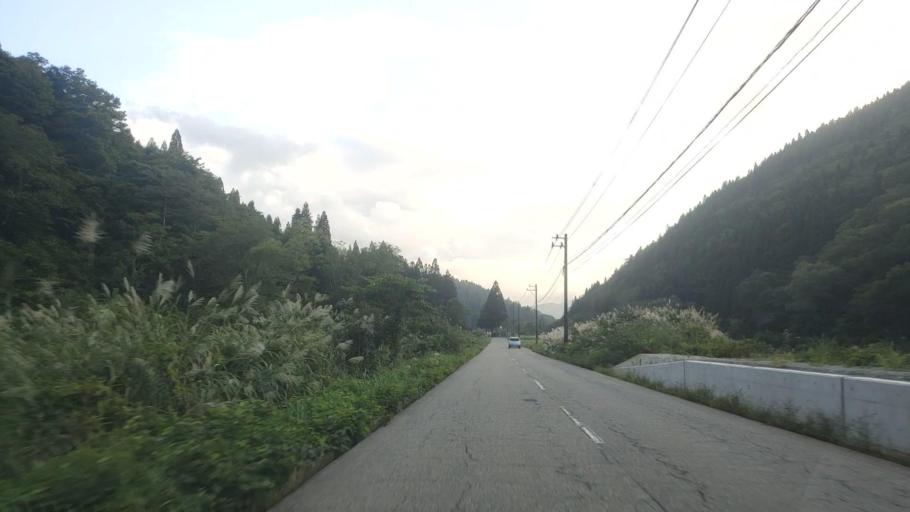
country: JP
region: Toyama
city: Yatsuomachi-higashikumisaka
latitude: 36.4728
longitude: 137.0492
